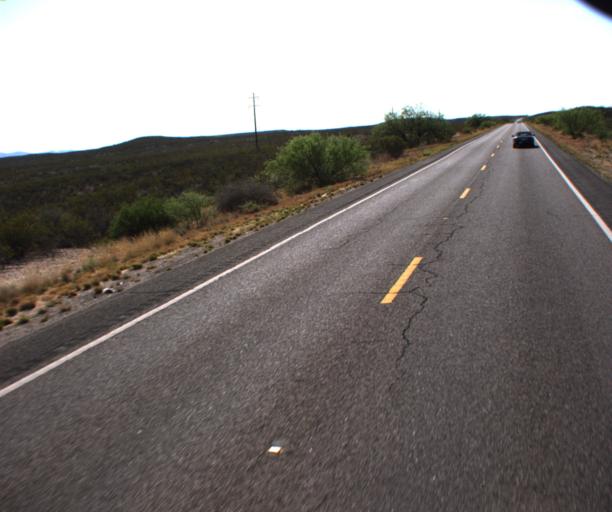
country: US
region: Arizona
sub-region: Cochise County
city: Tombstone
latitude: 31.7837
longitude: -110.1430
